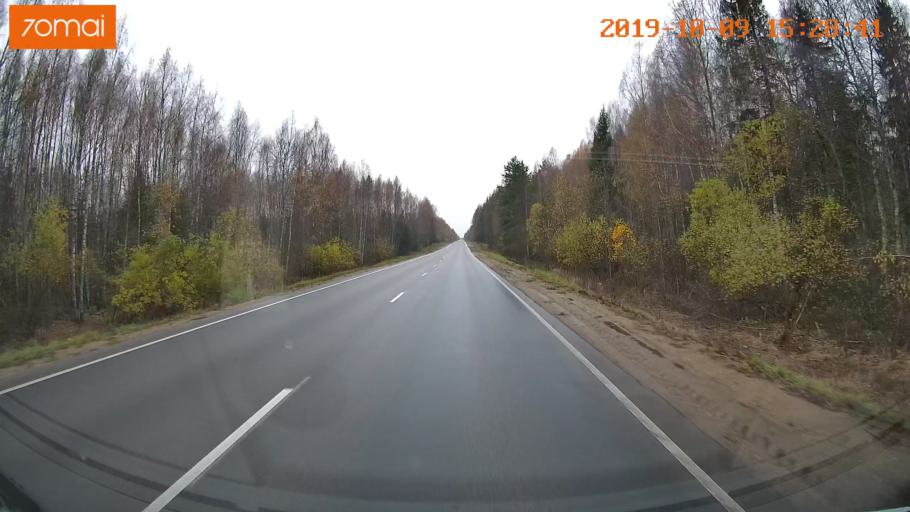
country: RU
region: Kostroma
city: Susanino
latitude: 58.0003
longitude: 41.3558
